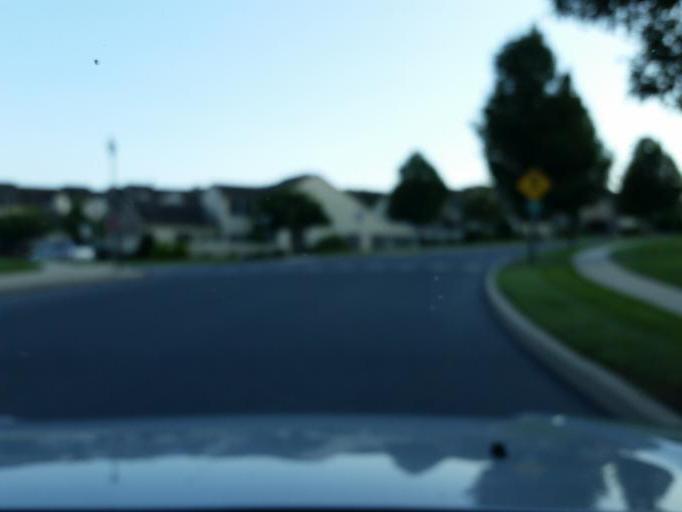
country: US
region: Pennsylvania
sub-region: Dauphin County
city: Hummelstown
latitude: 40.2457
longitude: -76.7185
